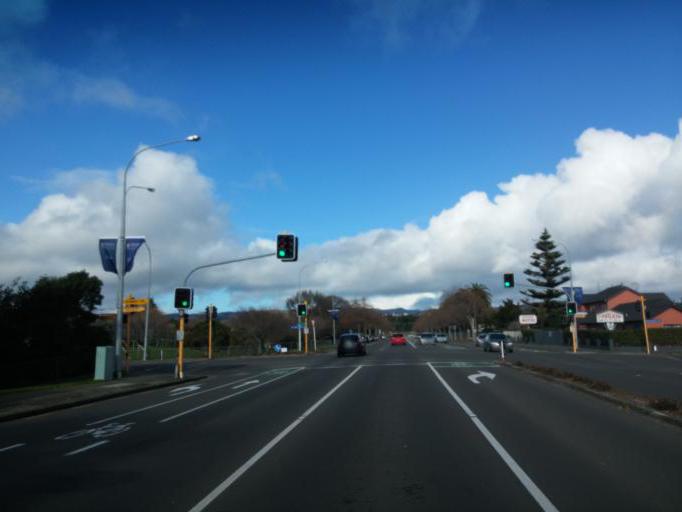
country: NZ
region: Manawatu-Wanganui
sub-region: Palmerston North City
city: Palmerston North
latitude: -40.3679
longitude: 175.6202
